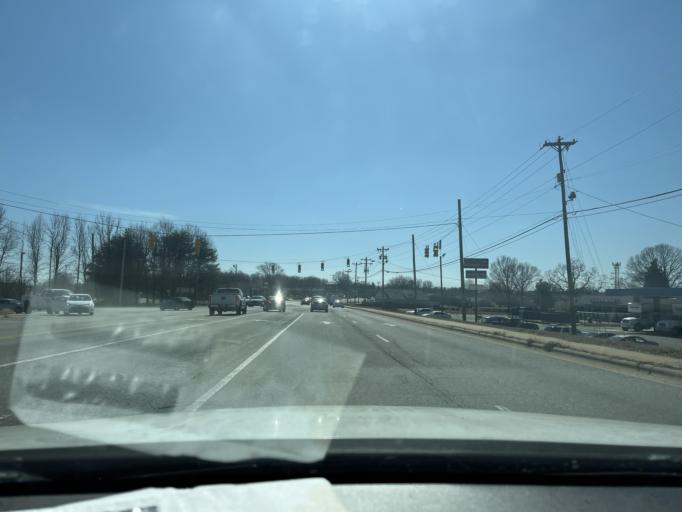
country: US
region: North Carolina
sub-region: Guilford County
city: Jamestown
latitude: 36.0619
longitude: -79.9081
